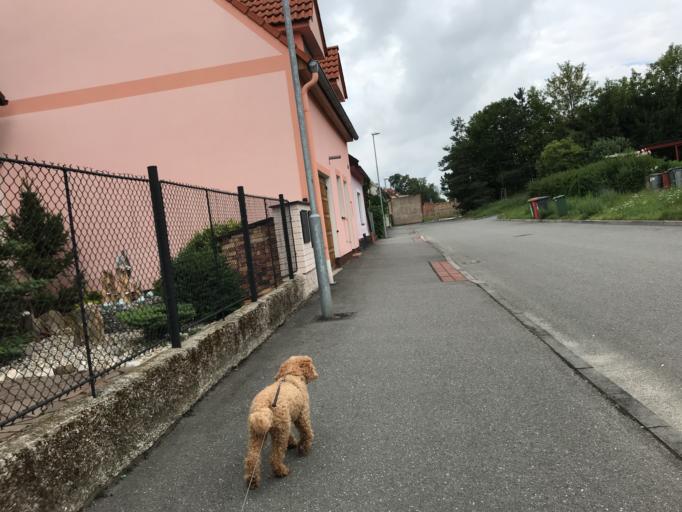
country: CZ
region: Jihocesky
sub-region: Okres Jindrichuv Hradec
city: Trebon
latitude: 49.0072
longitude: 14.7555
